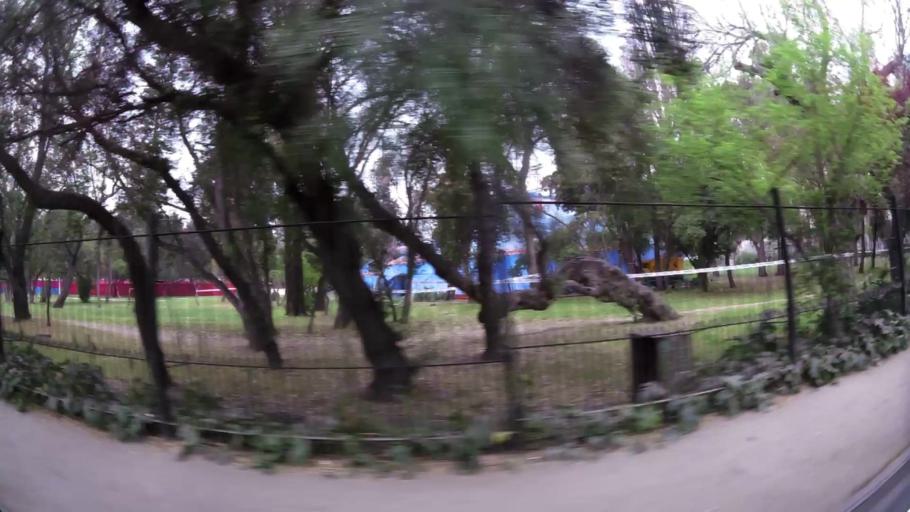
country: CL
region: Santiago Metropolitan
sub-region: Provincia de Santiago
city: Santiago
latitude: -33.4700
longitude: -70.6579
